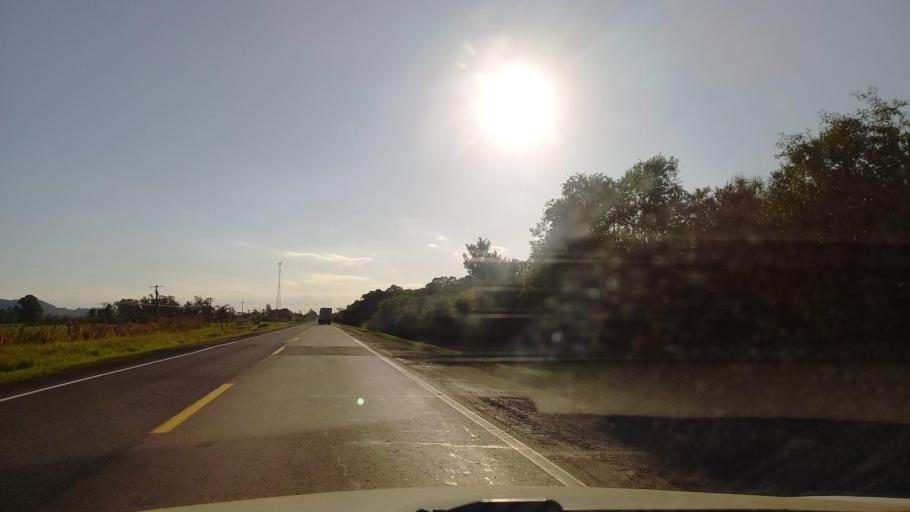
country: BR
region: Rio Grande do Sul
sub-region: Venancio Aires
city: Venancio Aires
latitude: -29.6678
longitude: -52.0434
